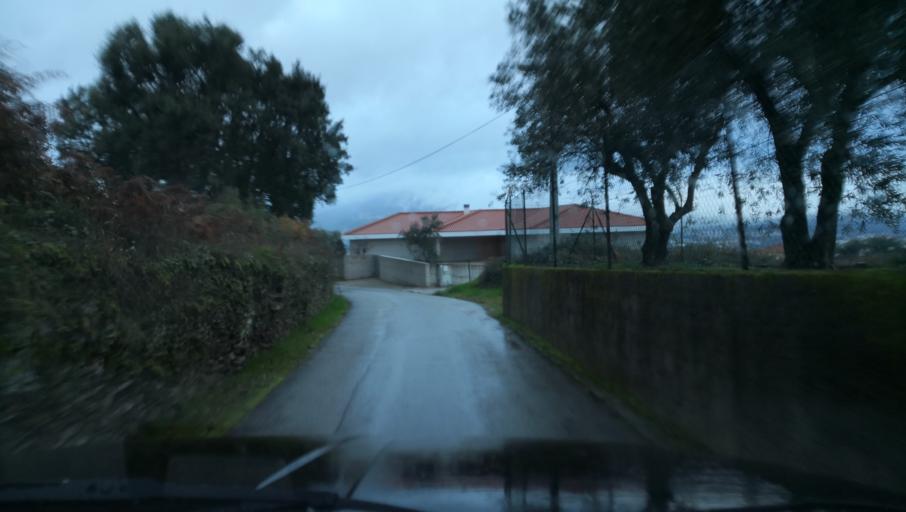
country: PT
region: Vila Real
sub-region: Vila Real
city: Vila Real
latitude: 41.2783
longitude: -7.7294
